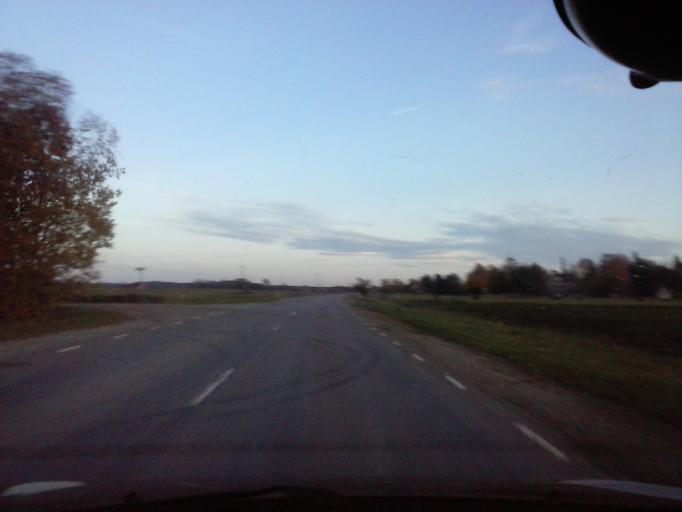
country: EE
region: Raplamaa
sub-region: Maerjamaa vald
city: Marjamaa
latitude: 58.9231
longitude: 24.4053
